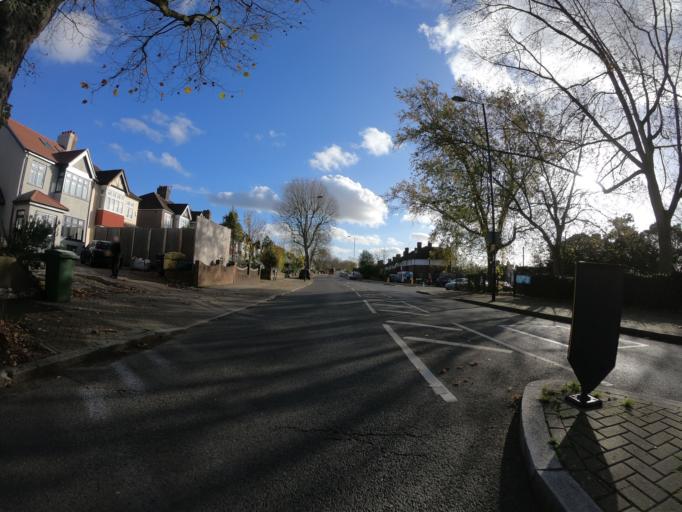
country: GB
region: England
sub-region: Greater London
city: Blackheath
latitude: 51.4419
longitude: 0.0155
